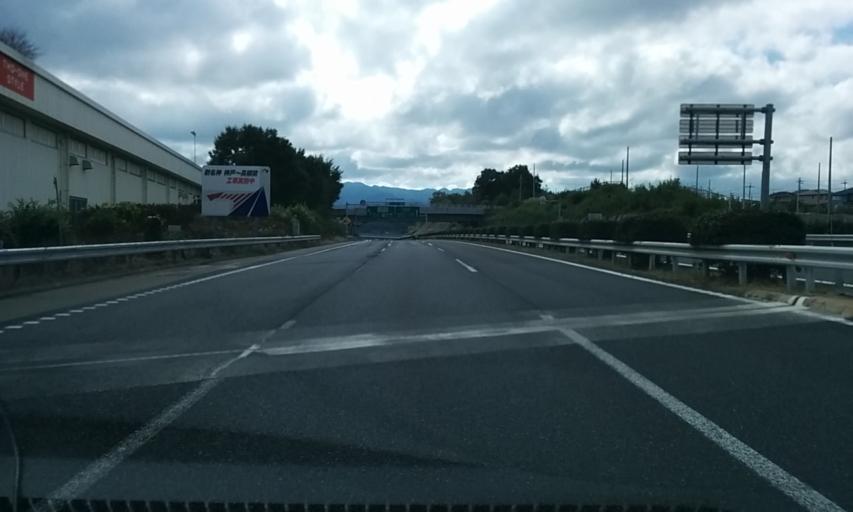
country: JP
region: Hyogo
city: Sandacho
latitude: 34.8579
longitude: 135.2163
